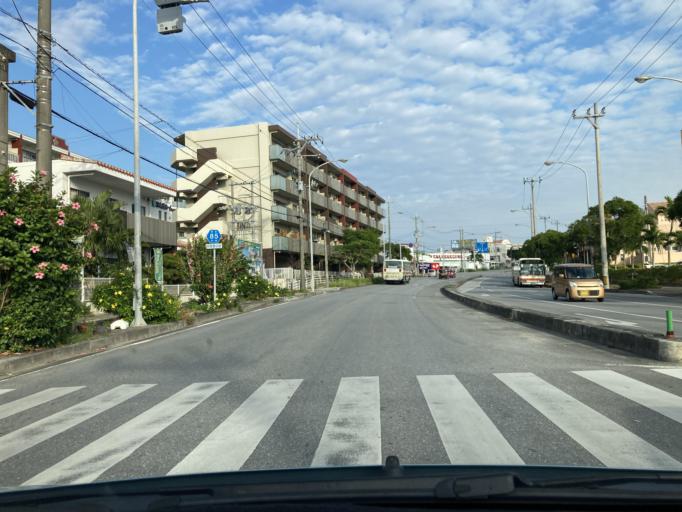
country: JP
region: Okinawa
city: Okinawa
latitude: 26.3537
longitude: 127.8245
